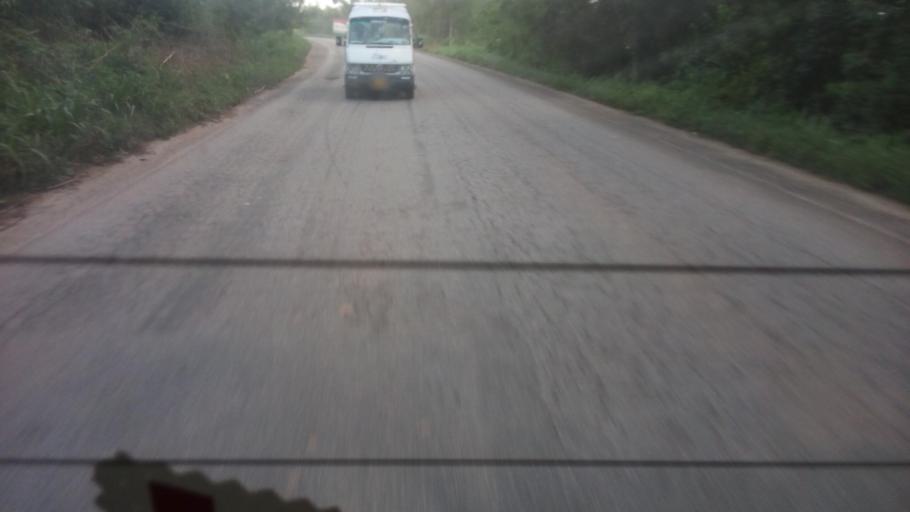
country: GH
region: Western
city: Tarkwa
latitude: 5.2006
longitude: -2.0291
